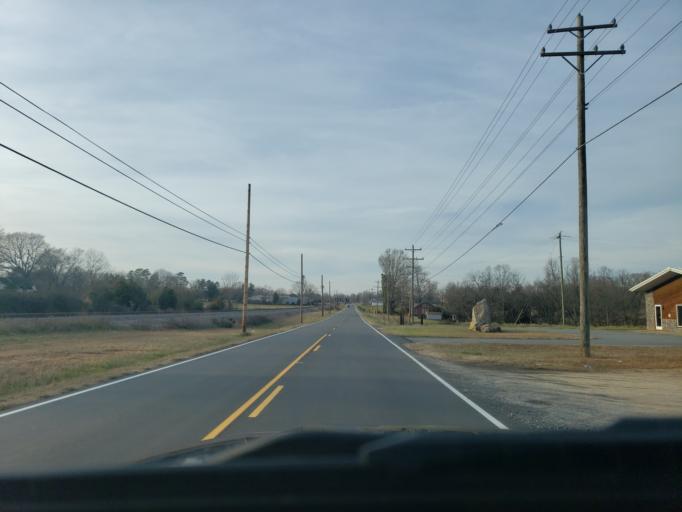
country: US
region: North Carolina
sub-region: Cleveland County
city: Boiling Springs
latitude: 35.3192
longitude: -81.7483
